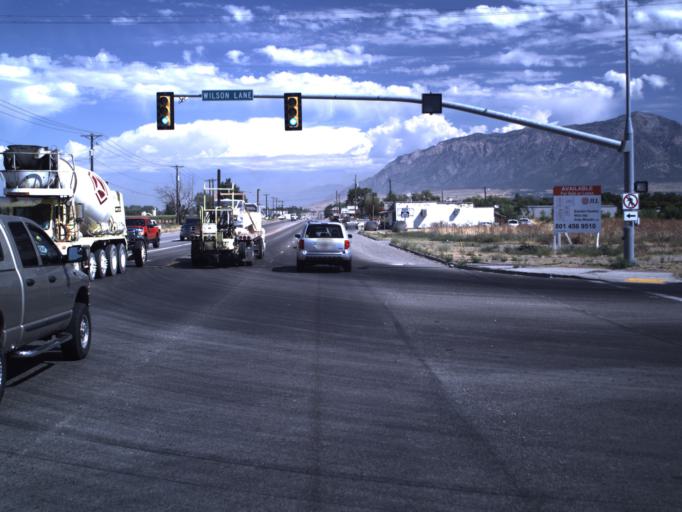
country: US
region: Utah
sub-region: Weber County
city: Marriott-Slaterville
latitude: 41.2286
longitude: -112.0255
